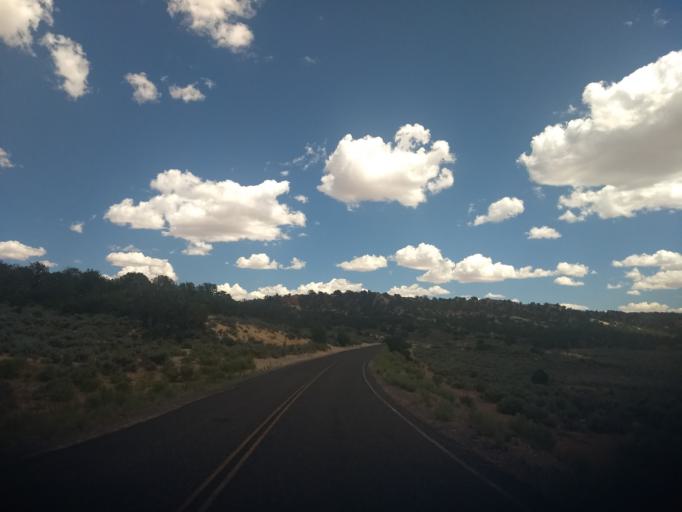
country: US
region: Utah
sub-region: Kane County
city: Kanab
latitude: 37.1226
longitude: -112.6783
